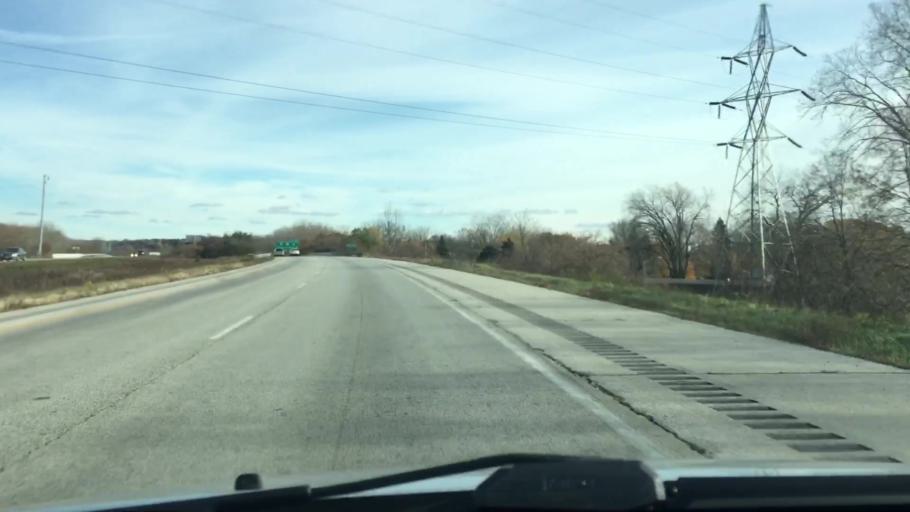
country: US
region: Wisconsin
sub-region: Brown County
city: Green Bay
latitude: 44.5203
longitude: -87.9699
